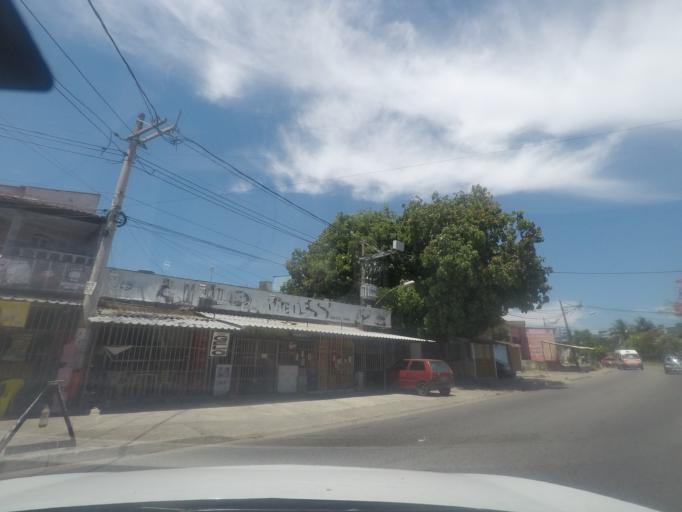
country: BR
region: Rio de Janeiro
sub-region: Itaguai
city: Itaguai
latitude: -22.9815
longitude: -43.6855
